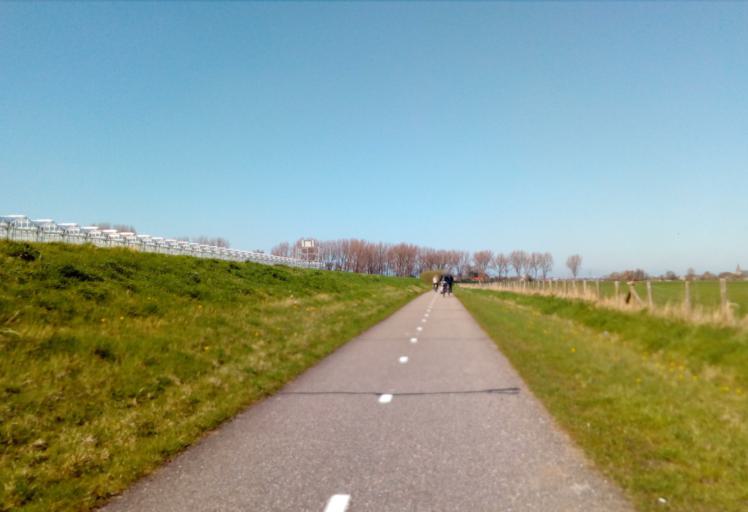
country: NL
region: South Holland
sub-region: Gemeente Westland
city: De Lier
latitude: 51.9858
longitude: 4.2911
